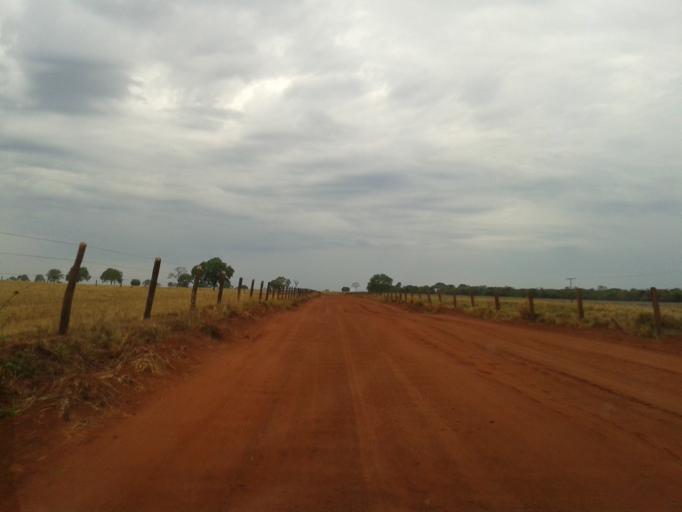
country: BR
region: Minas Gerais
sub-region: Ituiutaba
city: Ituiutaba
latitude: -18.9358
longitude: -49.7351
